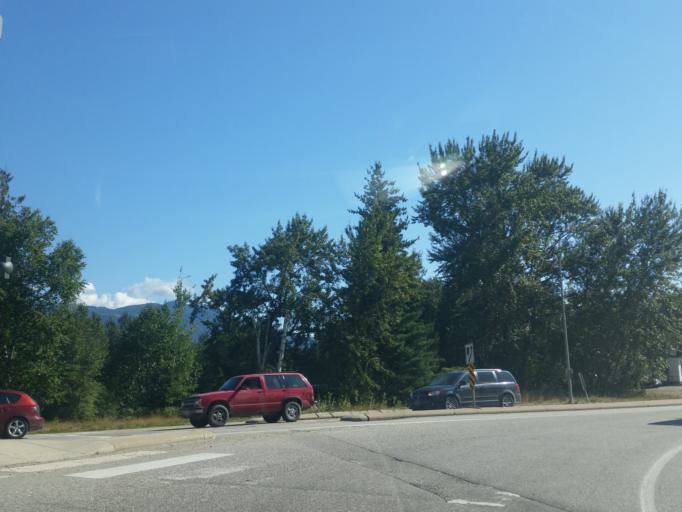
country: CA
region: British Columbia
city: Sicamous
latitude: 50.8379
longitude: -118.9764
